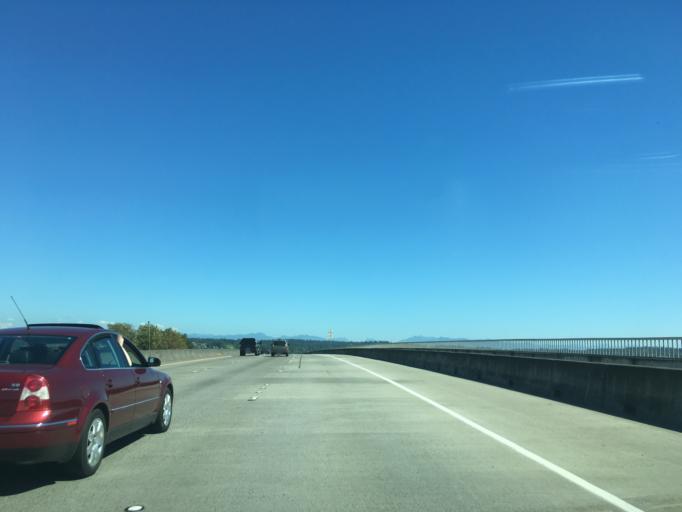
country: US
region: Washington
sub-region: Snohomish County
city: Everett
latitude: 47.9789
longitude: -122.1836
